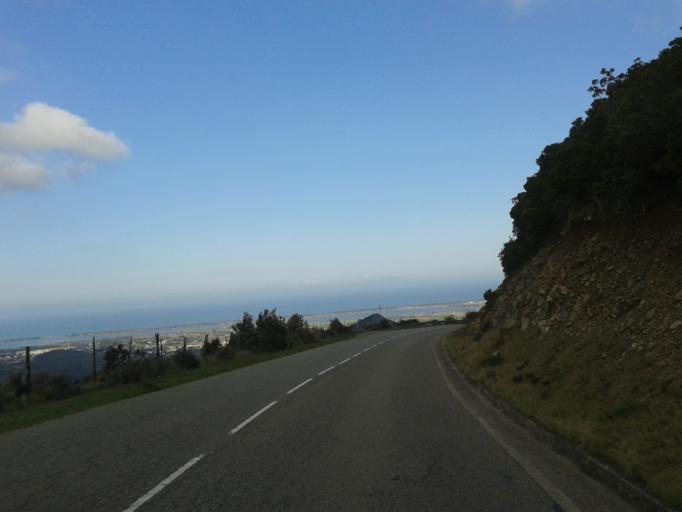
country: FR
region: Corsica
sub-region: Departement de la Haute-Corse
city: Biguglia
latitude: 42.5991
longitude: 9.4019
